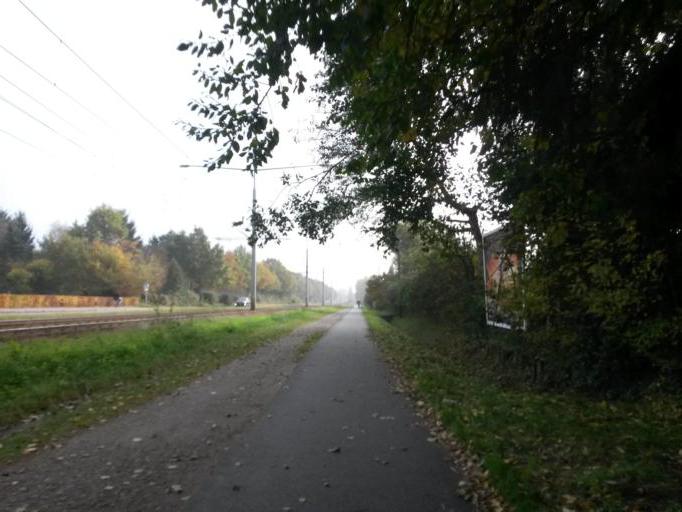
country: DE
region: Bremen
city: Bremen
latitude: 53.0784
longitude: 8.8617
